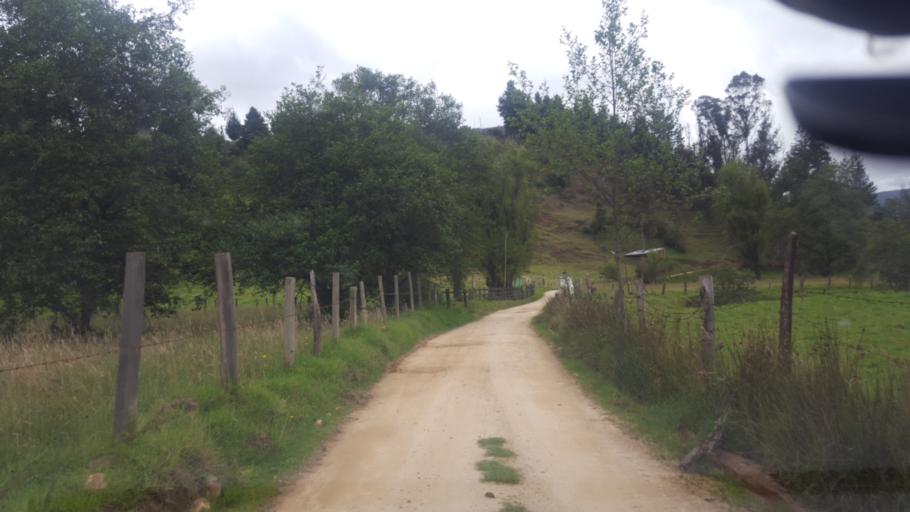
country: CO
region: Boyaca
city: Belen
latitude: 6.0135
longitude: -72.8649
